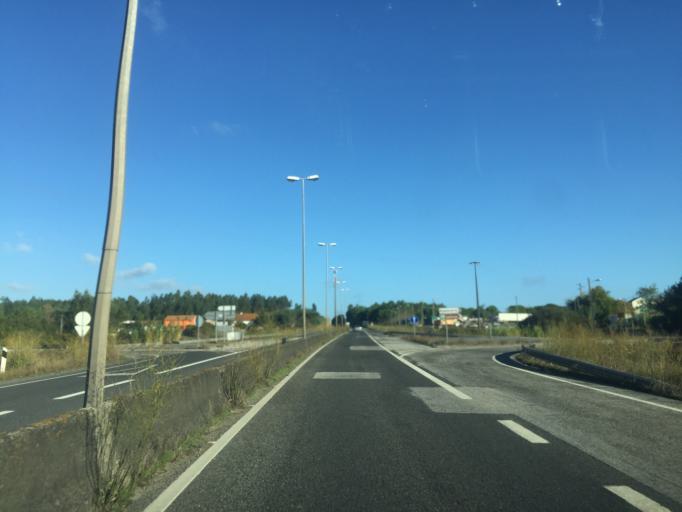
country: PT
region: Santarem
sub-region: Rio Maior
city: Rio Maior
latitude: 39.2818
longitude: -8.9415
